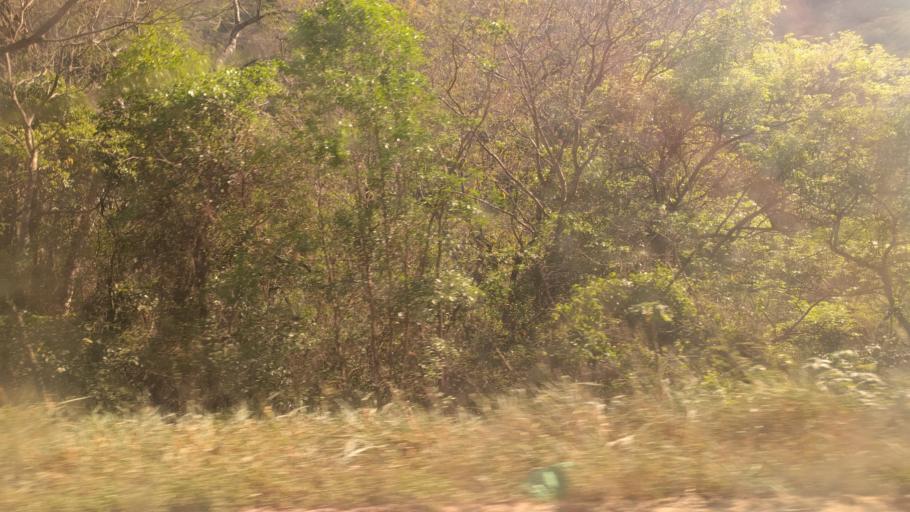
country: BO
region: Santa Cruz
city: Jorochito
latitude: -18.1784
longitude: -63.5747
